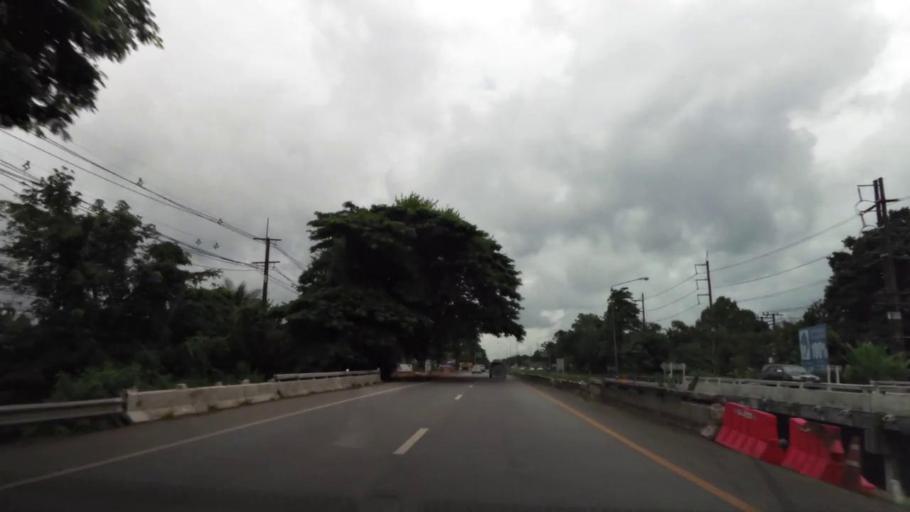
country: TH
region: Chanthaburi
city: Tha Mai
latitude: 12.6529
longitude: 102.0117
